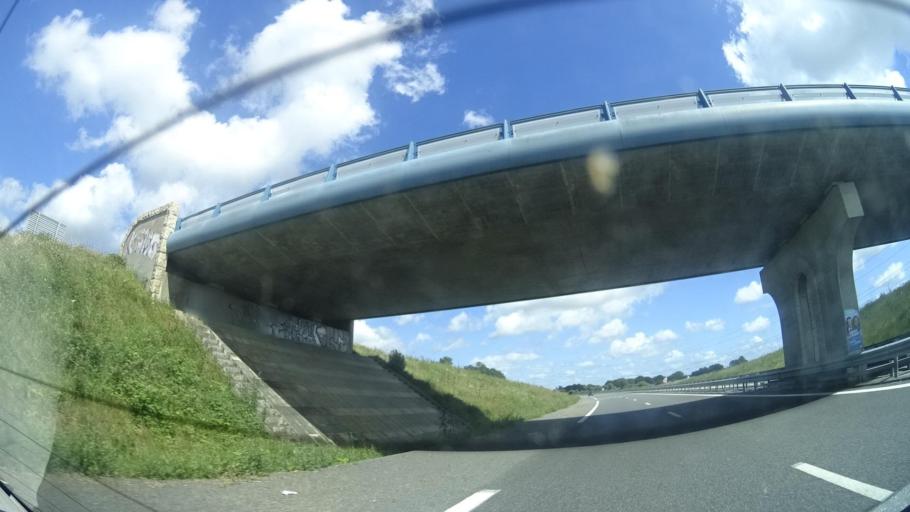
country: FR
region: Brittany
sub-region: Departement du Morbihan
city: Pluherlin
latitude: 47.6691
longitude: -2.3564
